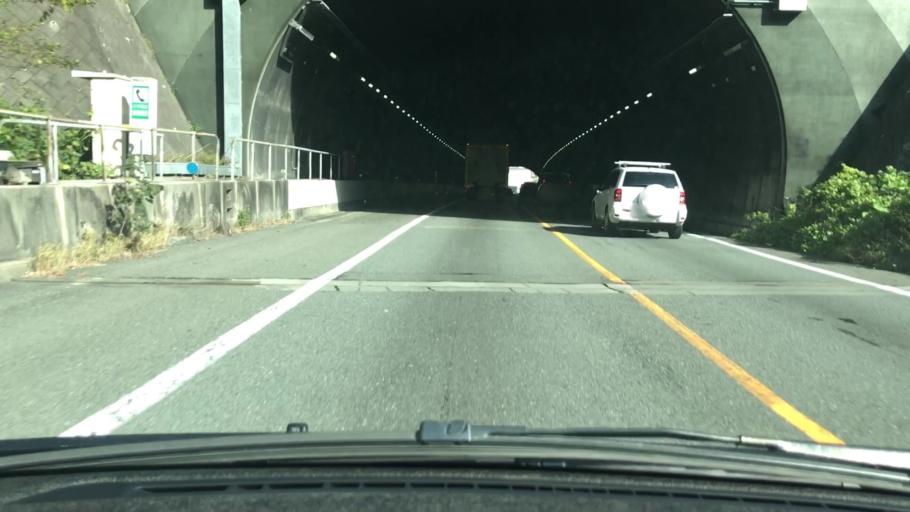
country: JP
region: Osaka
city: Takatsuki
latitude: 34.8749
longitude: 135.6534
